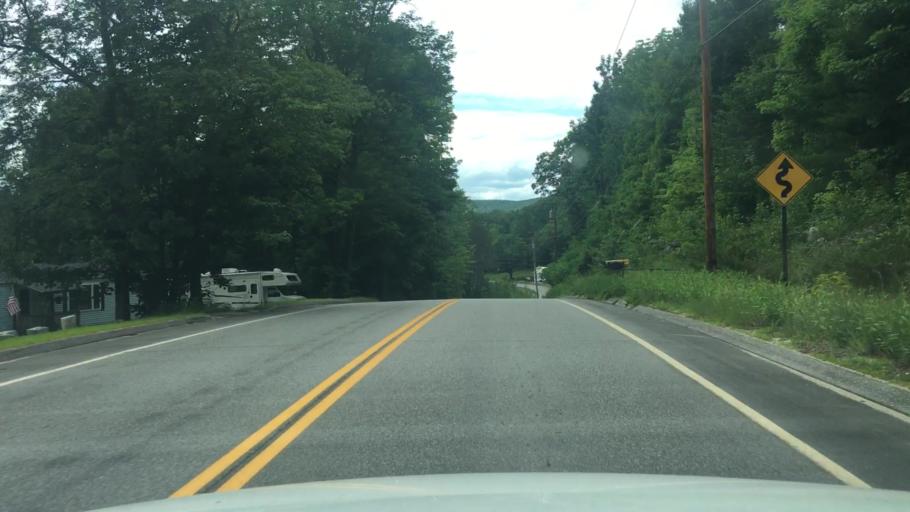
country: US
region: Maine
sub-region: Oxford County
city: Paris
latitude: 44.3689
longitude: -70.4643
